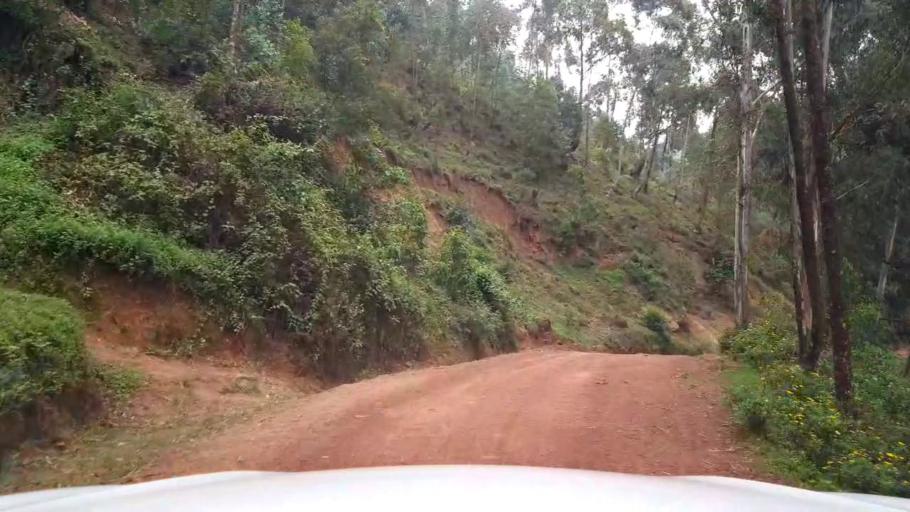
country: RW
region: Northern Province
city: Byumba
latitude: -1.4791
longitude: 29.9044
